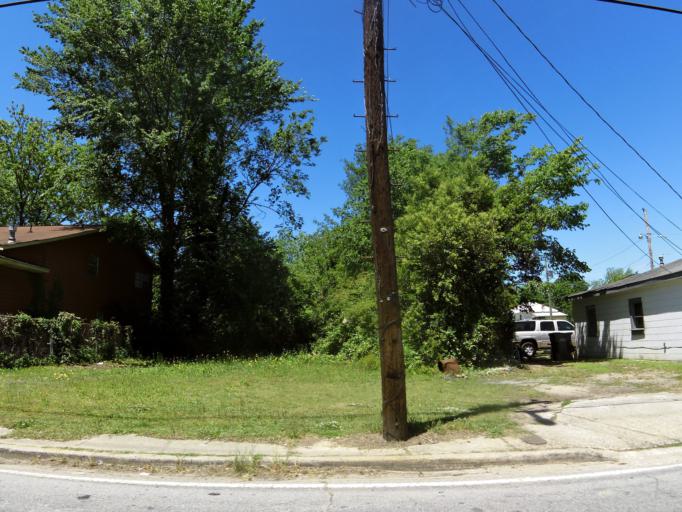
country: US
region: Georgia
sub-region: Richmond County
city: Augusta
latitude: 33.4576
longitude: -81.9821
